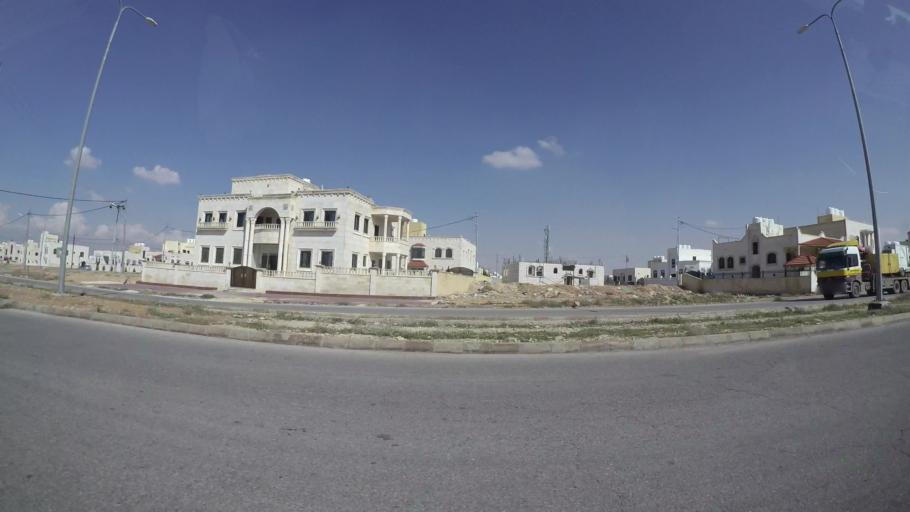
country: JO
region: Zarqa
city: Zarqa
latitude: 32.0604
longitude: 36.1127
